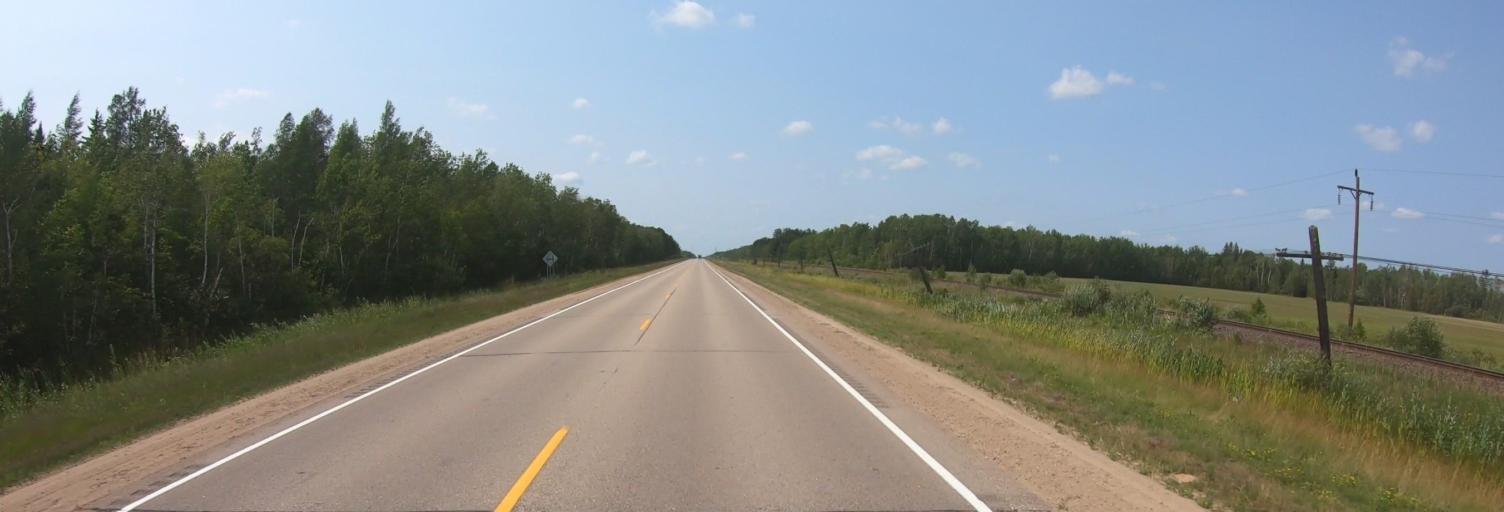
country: US
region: Minnesota
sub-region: Roseau County
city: Warroad
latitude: 48.7739
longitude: -94.9832
